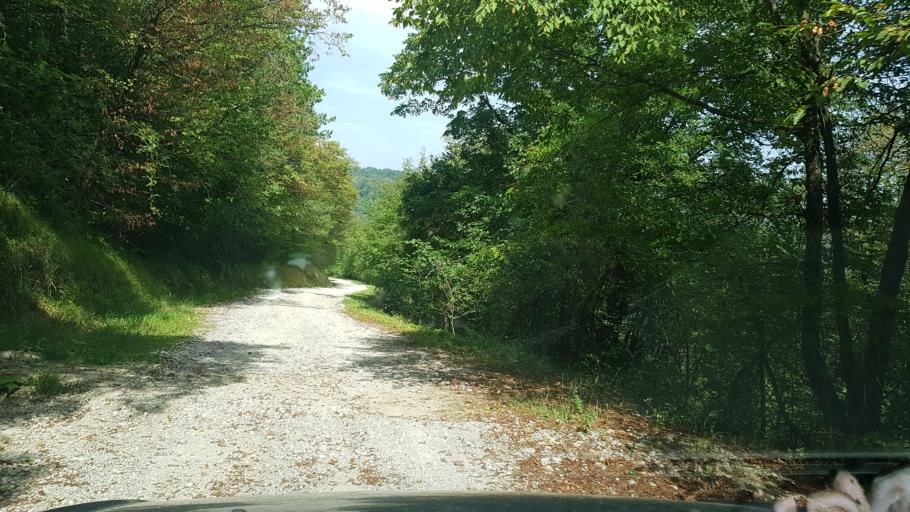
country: SI
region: Nova Gorica
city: Solkan
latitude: 46.0034
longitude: 13.6513
